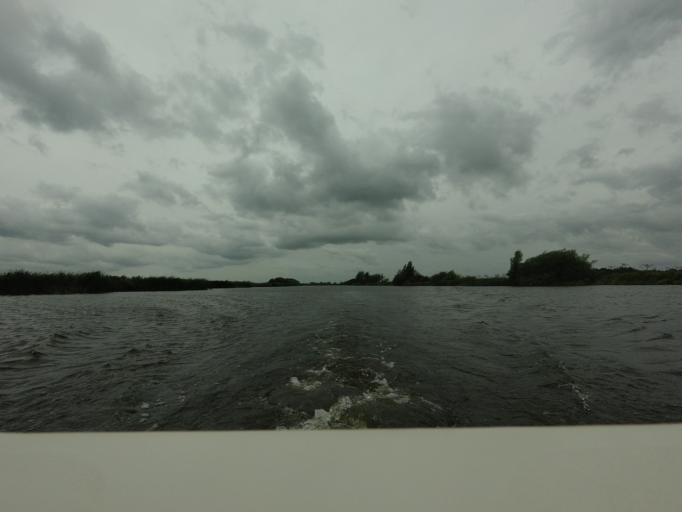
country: NL
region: Friesland
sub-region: Gemeente Boarnsterhim
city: Warten
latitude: 53.1012
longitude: 5.9104
